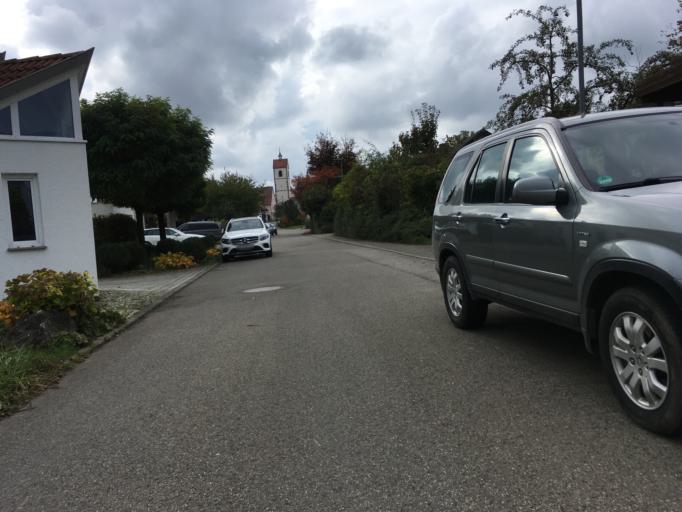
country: DE
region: Baden-Wuerttemberg
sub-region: Tuebingen Region
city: Kusterdingen
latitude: 48.4857
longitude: 9.1158
